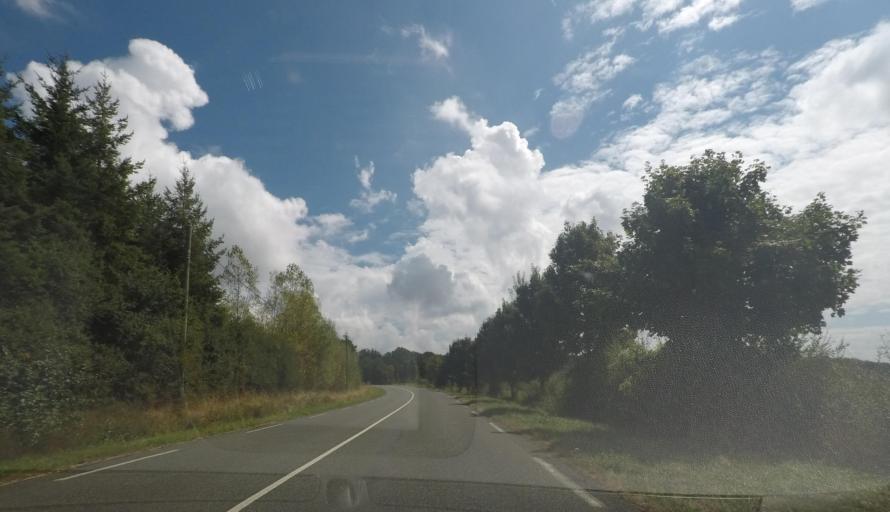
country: FR
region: Pays de la Loire
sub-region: Departement de la Sarthe
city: Saint-Cosme-en-Vairais
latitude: 48.2655
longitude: 0.5094
